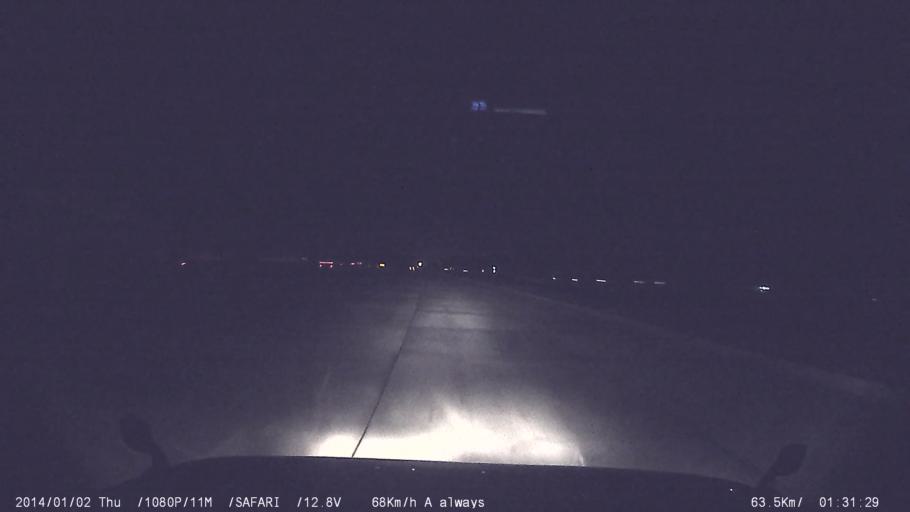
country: IN
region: Tamil Nadu
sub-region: Coimbatore
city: Sulur
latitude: 11.0943
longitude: 77.1494
